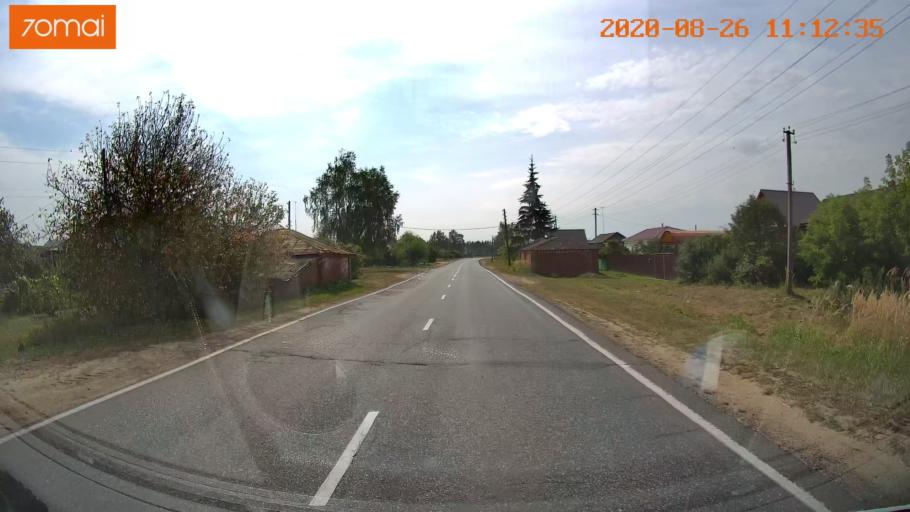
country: RU
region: Rjazan
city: Izhevskoye
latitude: 54.4688
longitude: 41.1249
